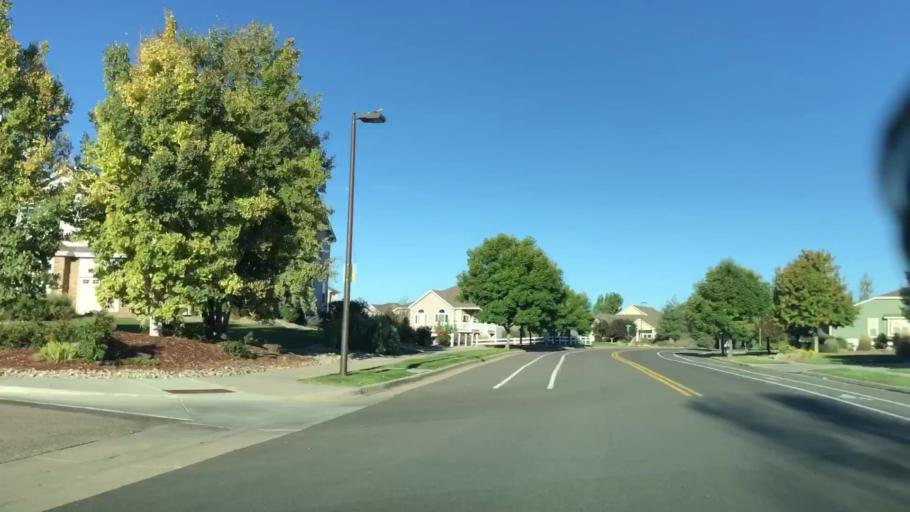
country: US
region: Colorado
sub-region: Larimer County
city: Loveland
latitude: 40.4611
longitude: -105.0334
